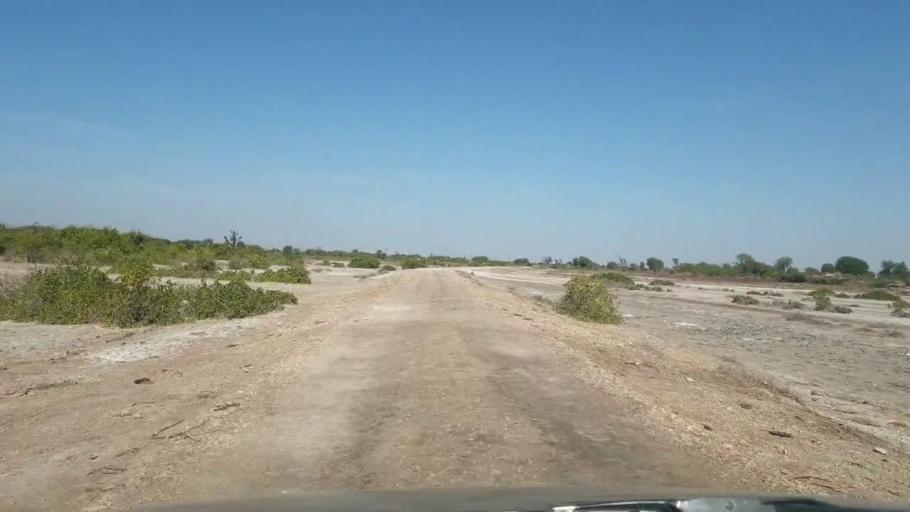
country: PK
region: Sindh
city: Dhoro Naro
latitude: 25.4097
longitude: 69.6166
